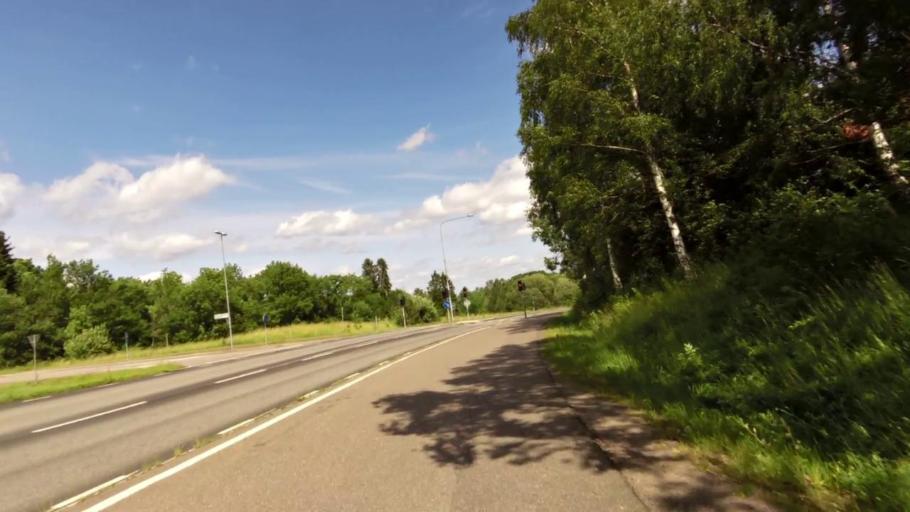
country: SE
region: OEstergoetland
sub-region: Linkopings Kommun
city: Malmslatt
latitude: 58.4223
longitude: 15.5665
